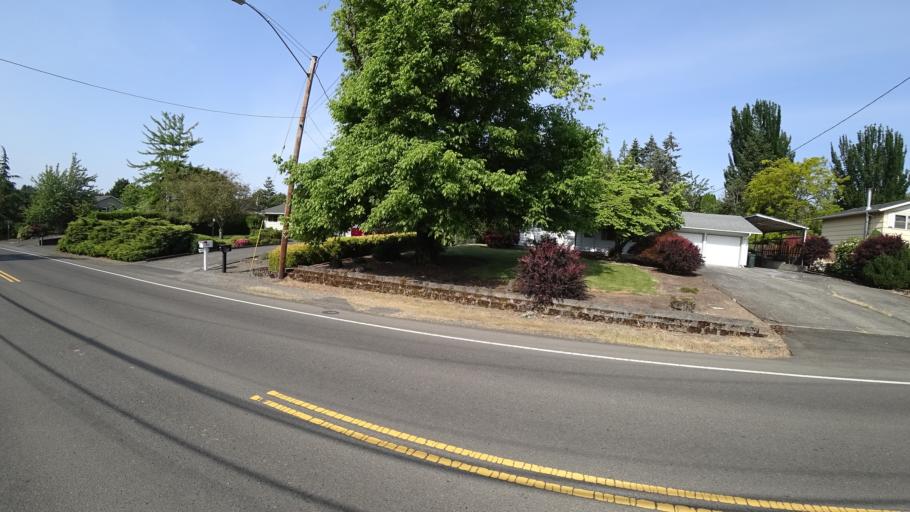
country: US
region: Oregon
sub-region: Clackamas County
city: Happy Valley
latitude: 45.4493
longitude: -122.5276
